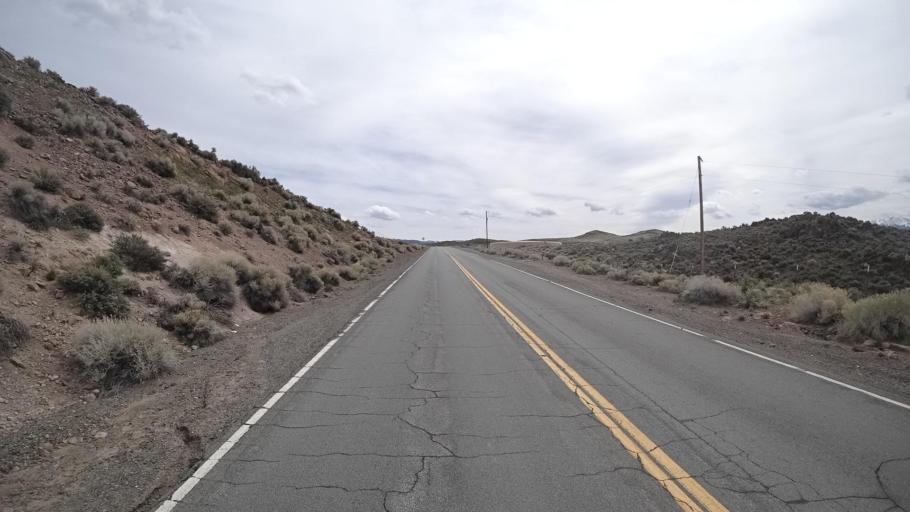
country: US
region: Nevada
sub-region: Washoe County
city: Sparks
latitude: 39.4692
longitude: -119.7549
